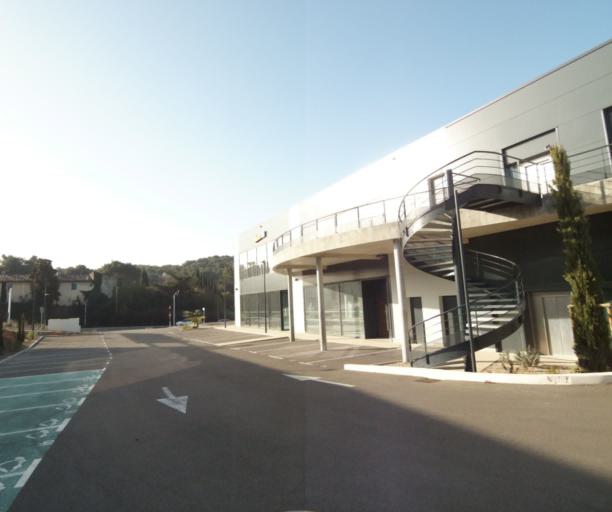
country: FR
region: Provence-Alpes-Cote d'Azur
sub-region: Departement des Bouches-du-Rhone
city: Septemes-les-Vallons
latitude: 43.4150
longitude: 5.3487
